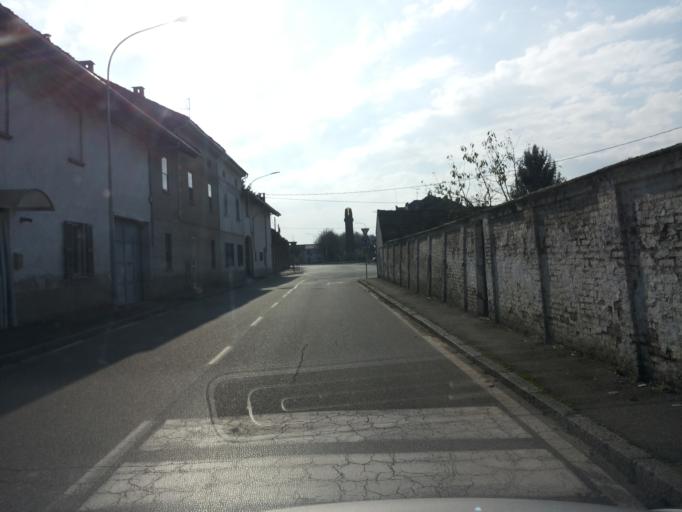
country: IT
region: Piedmont
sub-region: Provincia di Vercelli
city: Caresana
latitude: 45.2229
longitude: 8.5028
